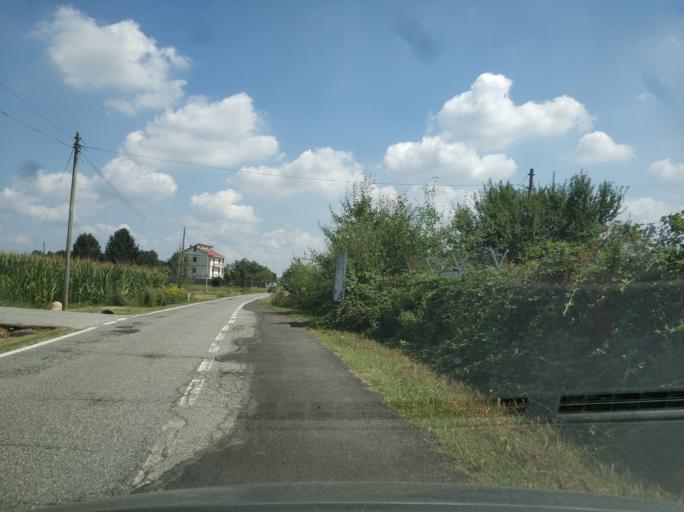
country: IT
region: Piedmont
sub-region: Provincia di Torino
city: San Francesco al Campo
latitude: 45.2503
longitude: 7.6701
